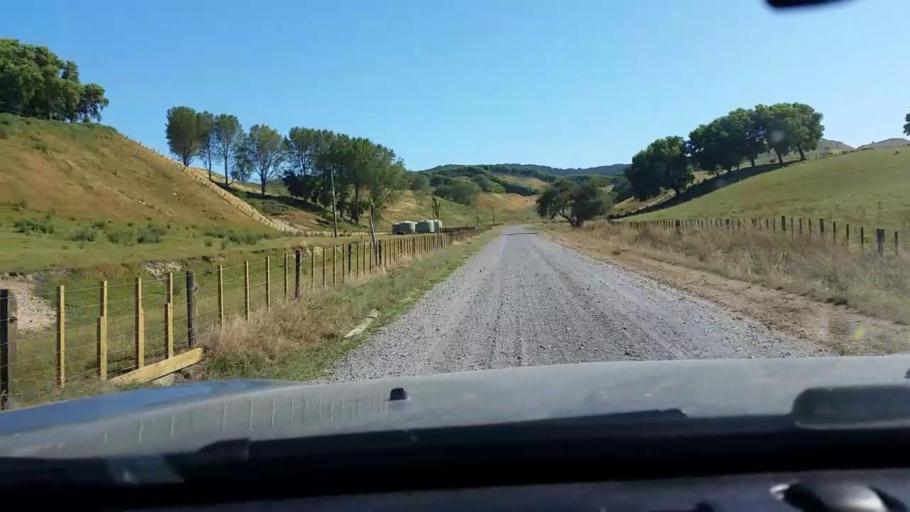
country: NZ
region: Bay of Plenty
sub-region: Rotorua District
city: Rotorua
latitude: -38.3148
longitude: 176.3020
